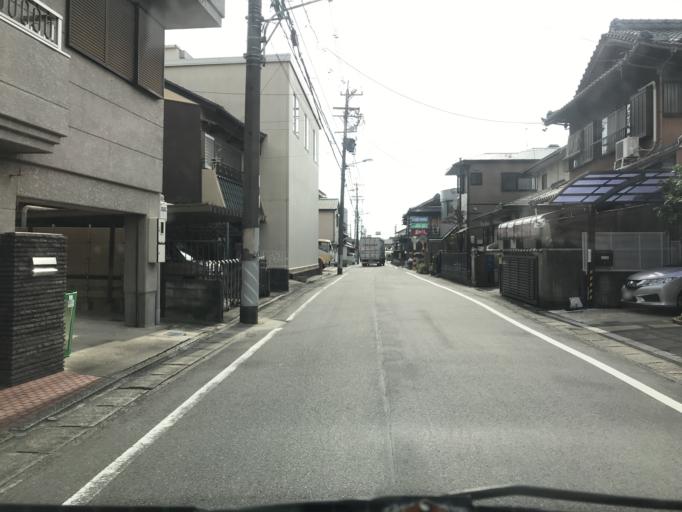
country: JP
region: Aichi
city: Inazawa
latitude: 35.2134
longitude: 136.8401
